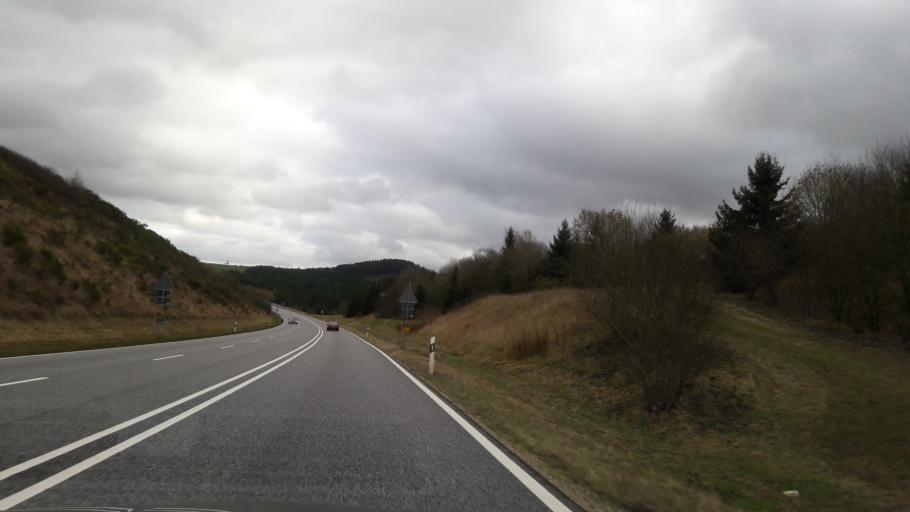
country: DE
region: Rheinland-Pfalz
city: Habscheid
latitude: 50.1982
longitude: 6.2757
